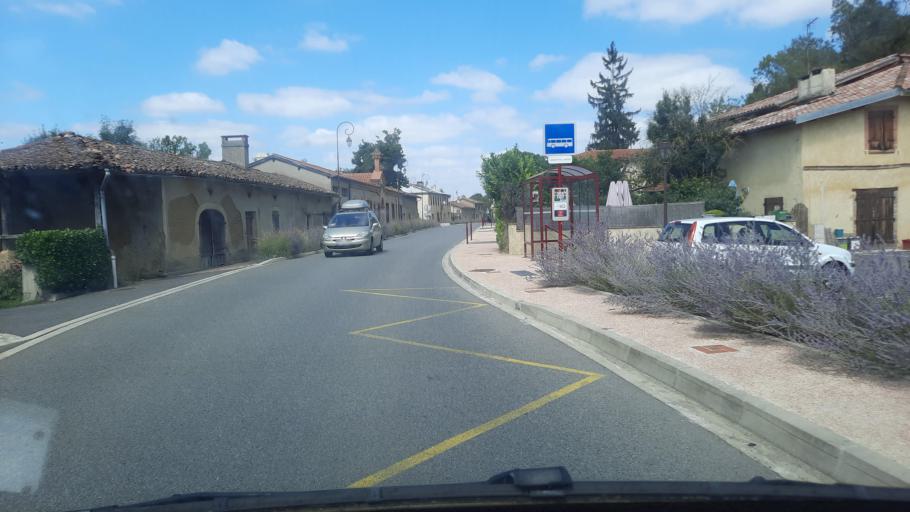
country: FR
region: Midi-Pyrenees
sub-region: Departement du Gers
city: Samatan
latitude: 43.5193
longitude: 0.9808
